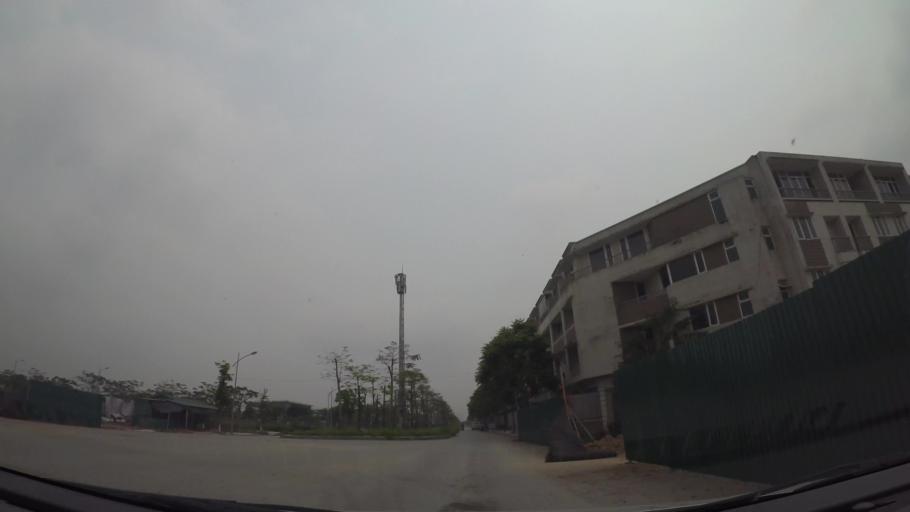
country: VN
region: Ha Noi
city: Ha Dong
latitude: 20.9746
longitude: 105.7511
